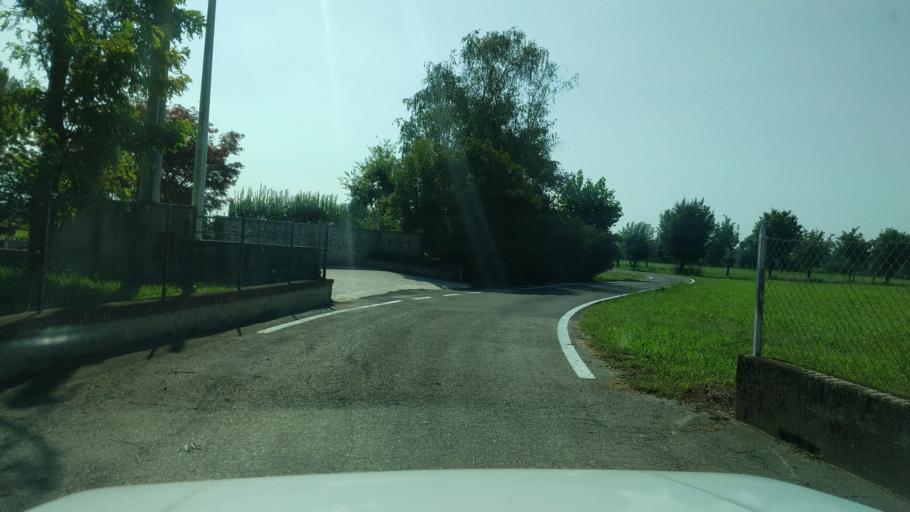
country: IT
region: Veneto
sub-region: Provincia di Vicenza
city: Schiavon
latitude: 45.7085
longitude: 11.6441
